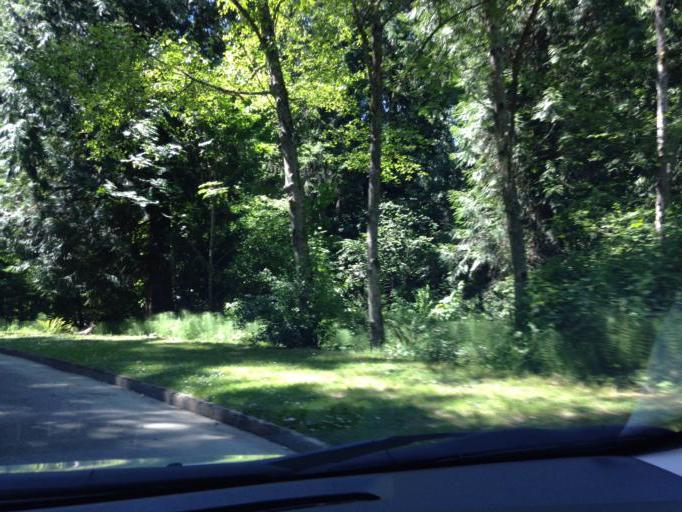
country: US
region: Washington
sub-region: King County
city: Mercer Island
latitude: 47.5529
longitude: -122.2498
